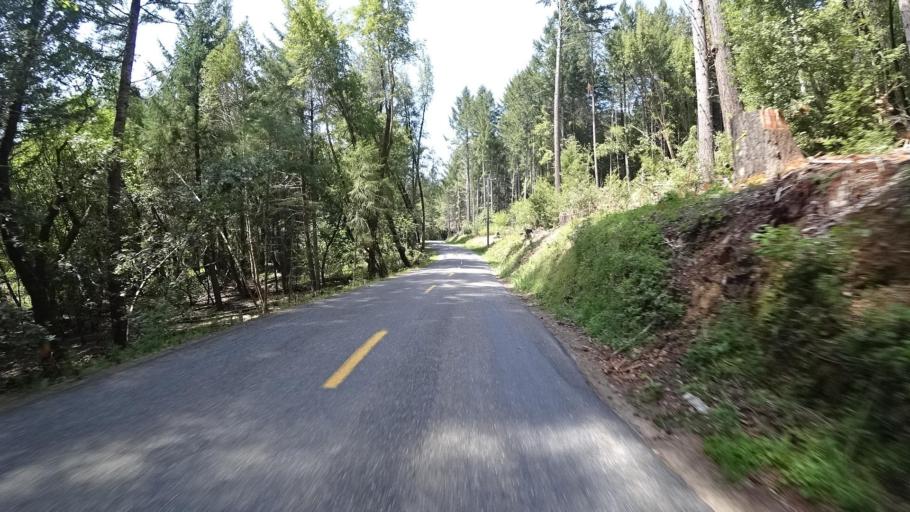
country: US
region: California
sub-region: Humboldt County
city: Redway
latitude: 40.3572
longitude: -123.7229
